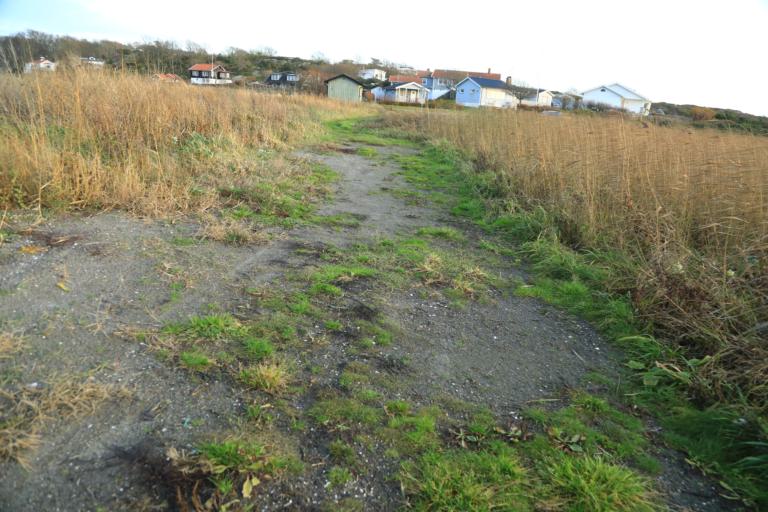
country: SE
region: Halland
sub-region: Varbergs Kommun
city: Varberg
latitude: 57.1902
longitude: 12.2043
